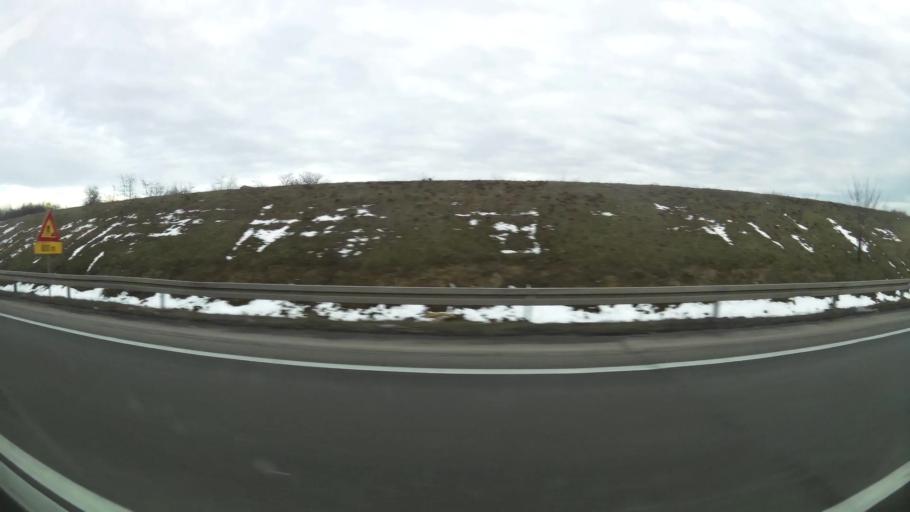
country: RS
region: Central Serbia
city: Sremcica
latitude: 44.7137
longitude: 20.3863
